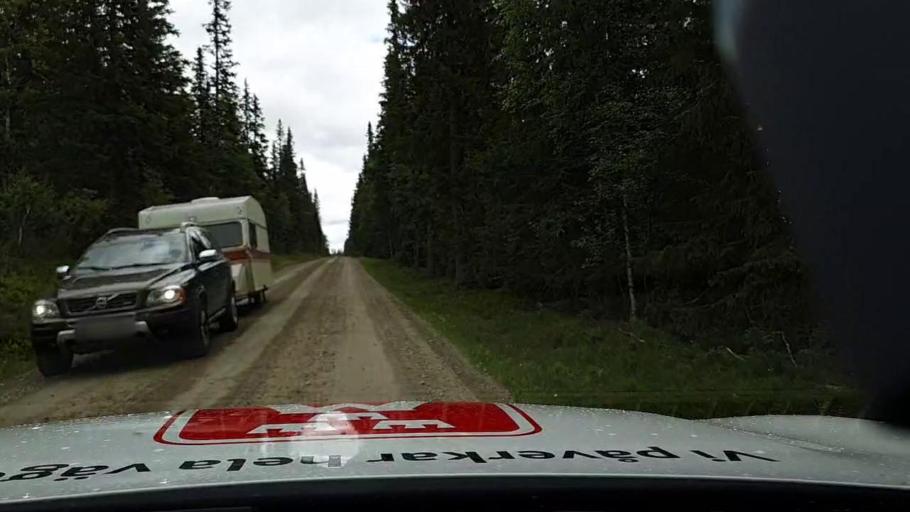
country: SE
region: Jaemtland
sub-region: Are Kommun
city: Jarpen
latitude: 62.6031
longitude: 13.2257
